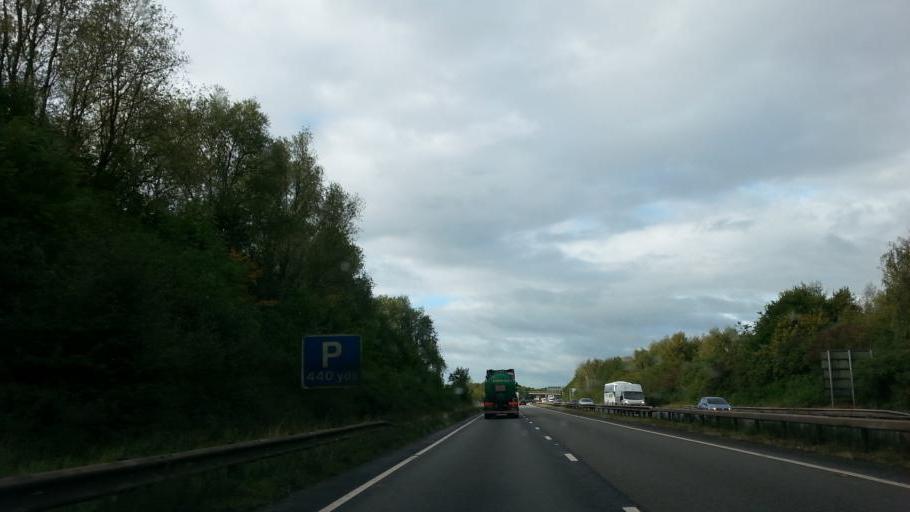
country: GB
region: England
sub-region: Leicestershire
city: Ashby de la Zouch
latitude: 52.7409
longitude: -1.4580
